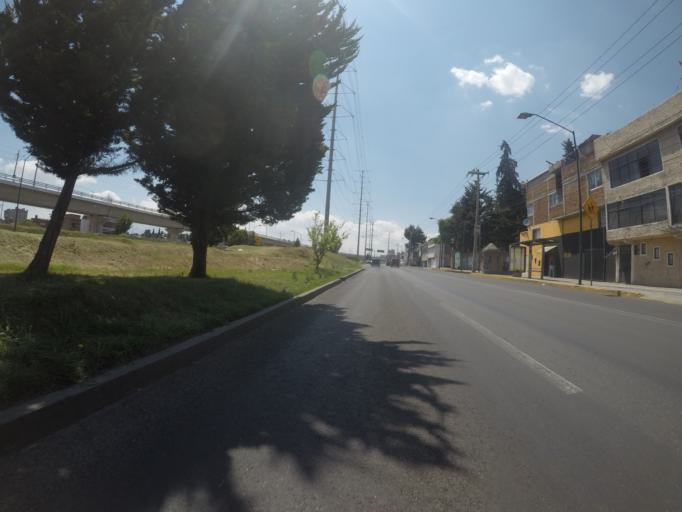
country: MX
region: Mexico
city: Toluca
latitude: 19.2691
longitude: -99.6490
